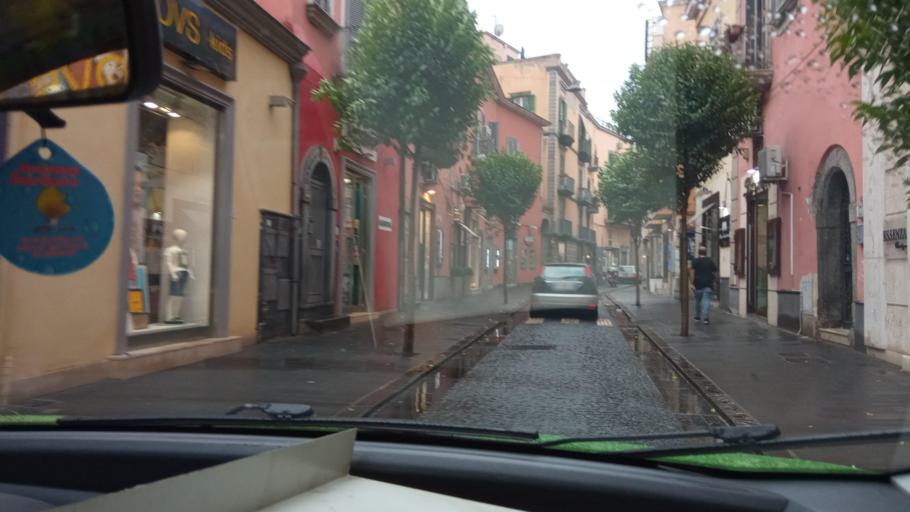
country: IT
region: Campania
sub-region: Provincia di Napoli
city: Pozzuoli
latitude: 40.8235
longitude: 14.1217
